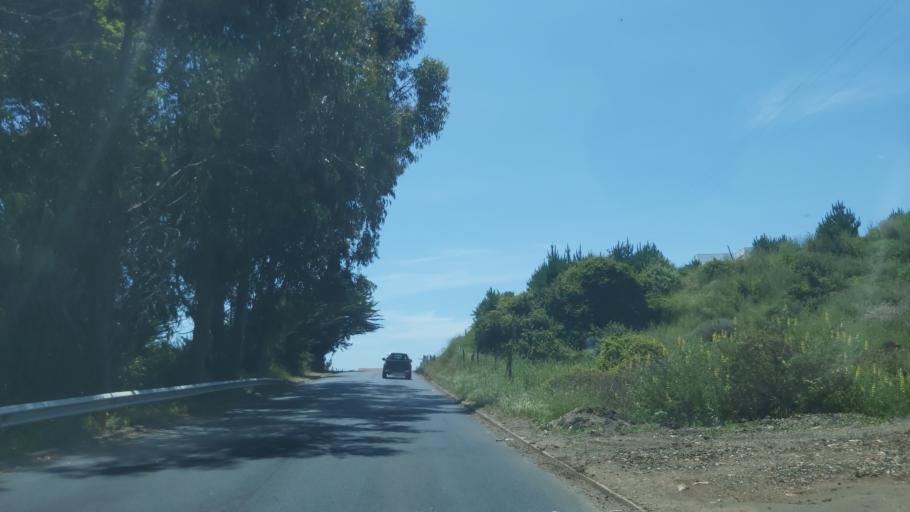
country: CL
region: Maule
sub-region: Provincia de Cauquenes
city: Cauquenes
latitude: -35.8282
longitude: -72.6146
